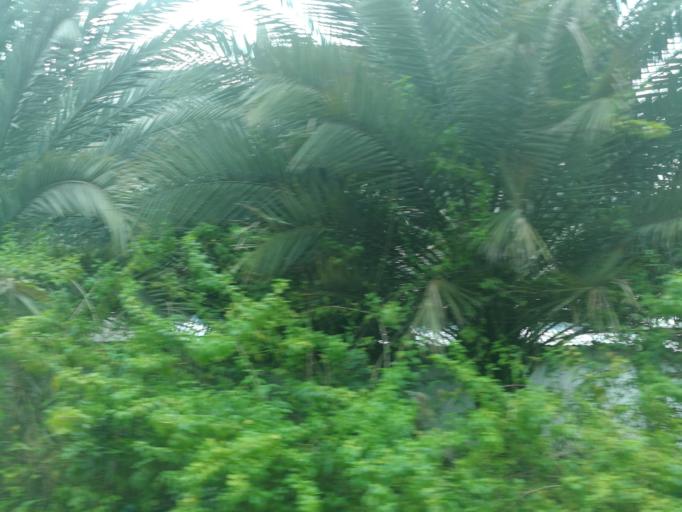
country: NG
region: Lagos
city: Ikoyi
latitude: 6.4336
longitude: 3.4165
